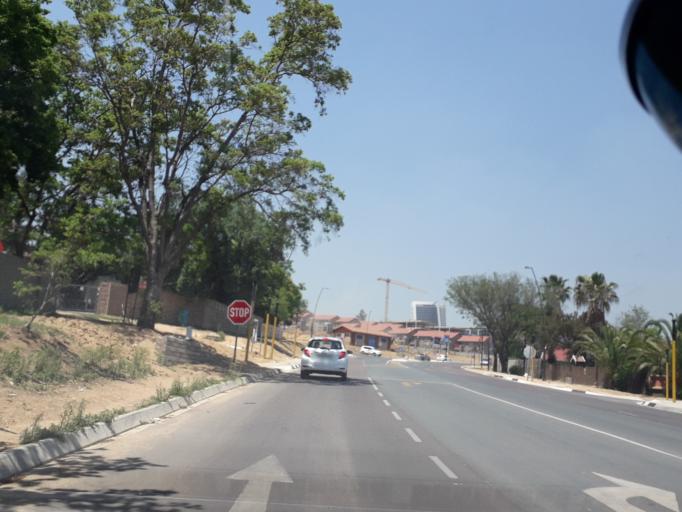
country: ZA
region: Gauteng
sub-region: City of Johannesburg Metropolitan Municipality
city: Midrand
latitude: -26.0059
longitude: 28.1044
